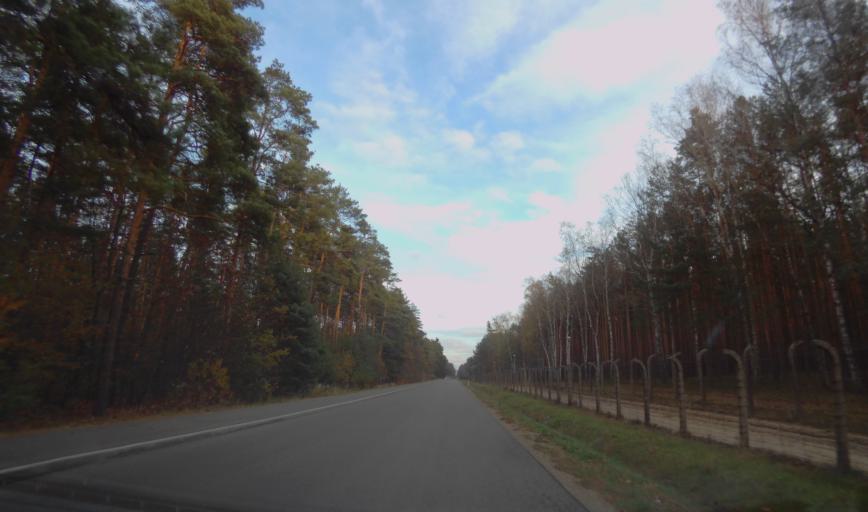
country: PL
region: Subcarpathian Voivodeship
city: Nowa Sarzyna
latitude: 50.3304
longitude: 22.3156
